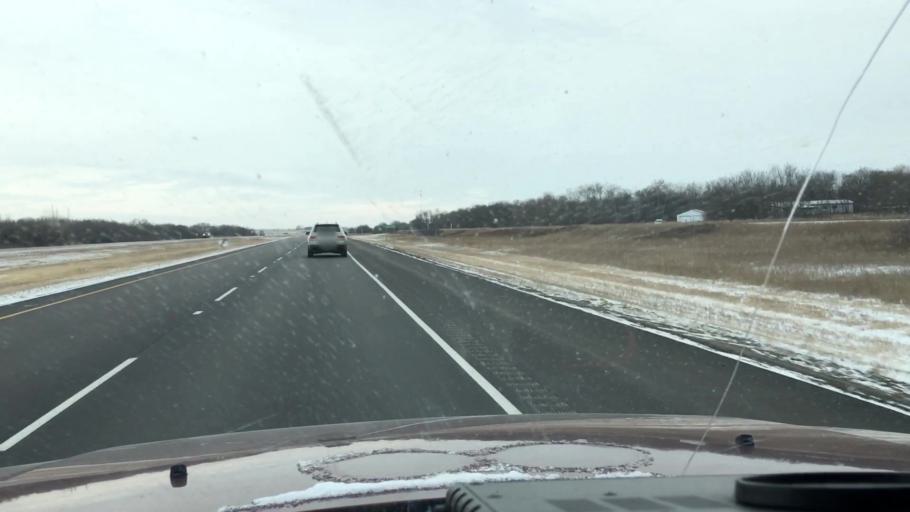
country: CA
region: Saskatchewan
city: Saskatoon
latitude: 51.8773
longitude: -106.5109
